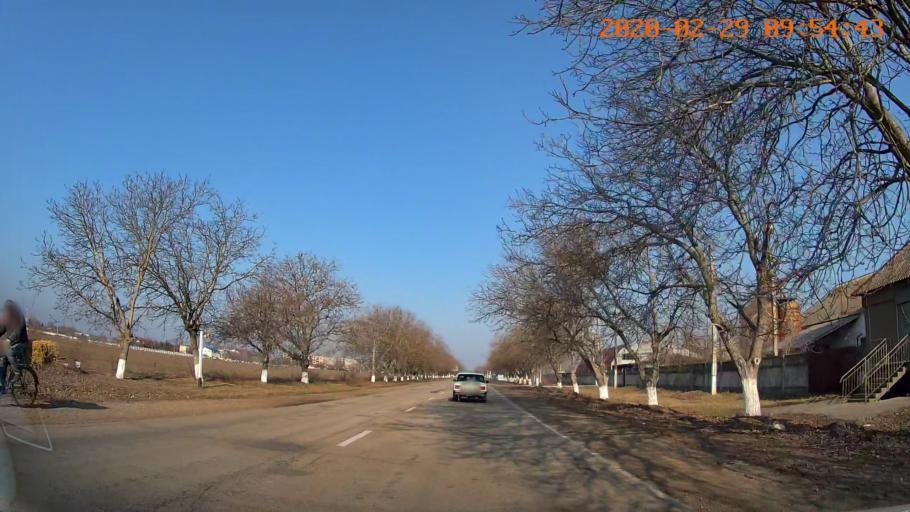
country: MD
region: Telenesti
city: Slobozia
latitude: 46.7306
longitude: 29.7141
